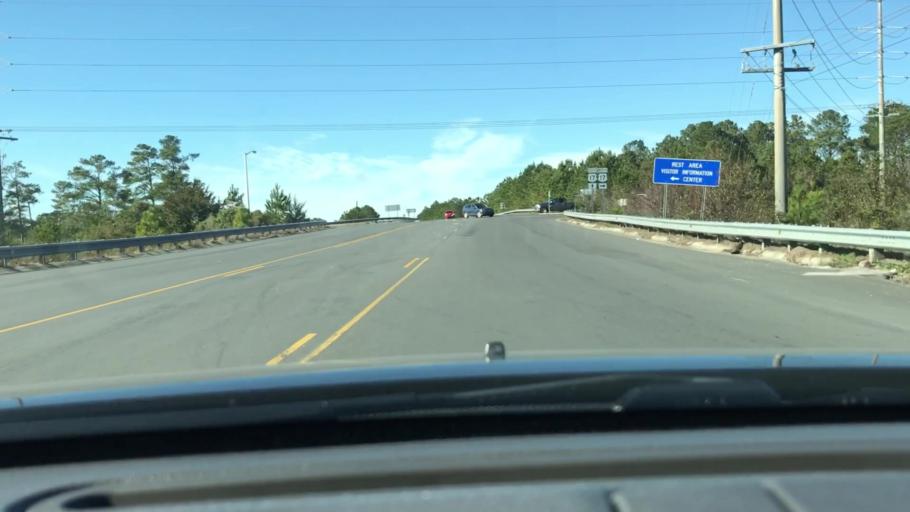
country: US
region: North Carolina
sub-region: Brunswick County
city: Shallotte
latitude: 33.9749
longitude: -78.4023
